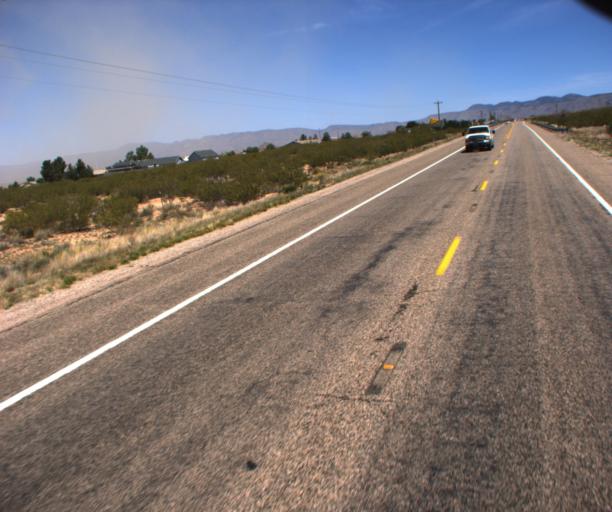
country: US
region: Arizona
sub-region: Mohave County
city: New Kingman-Butler
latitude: 35.3783
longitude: -113.8564
